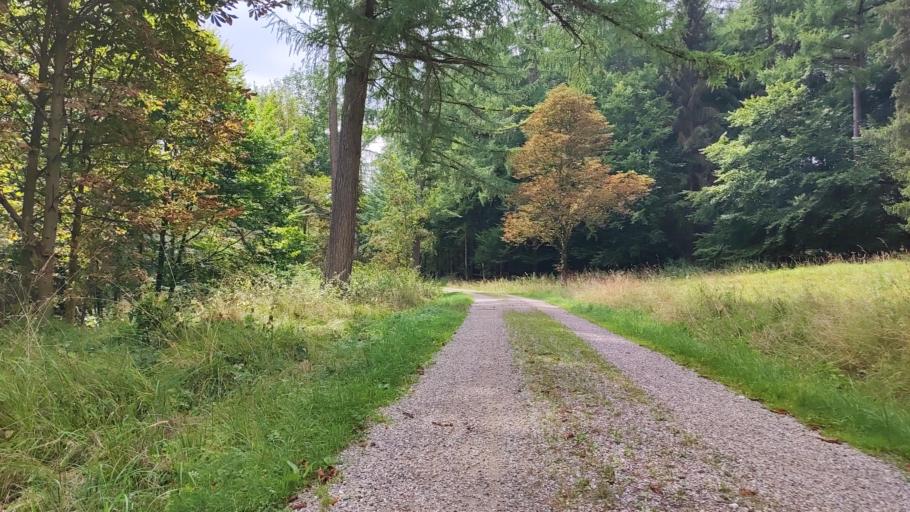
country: DE
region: Bavaria
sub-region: Swabia
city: Landensberg
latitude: 48.4231
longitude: 10.5100
